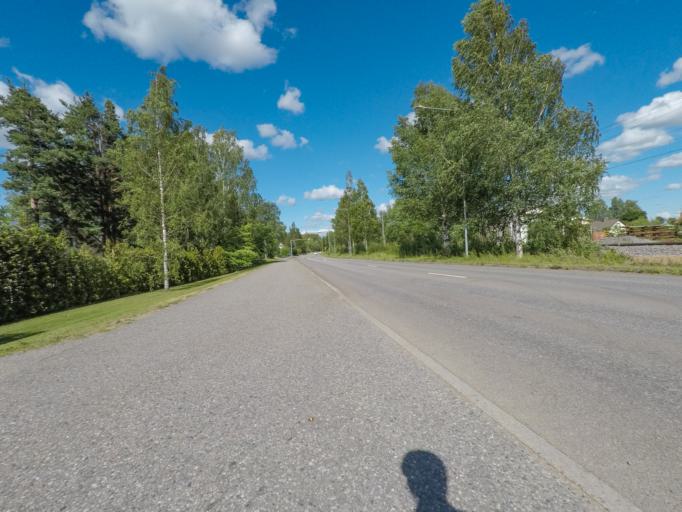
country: FI
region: South Karelia
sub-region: Lappeenranta
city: Lappeenranta
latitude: 61.0719
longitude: 28.2670
